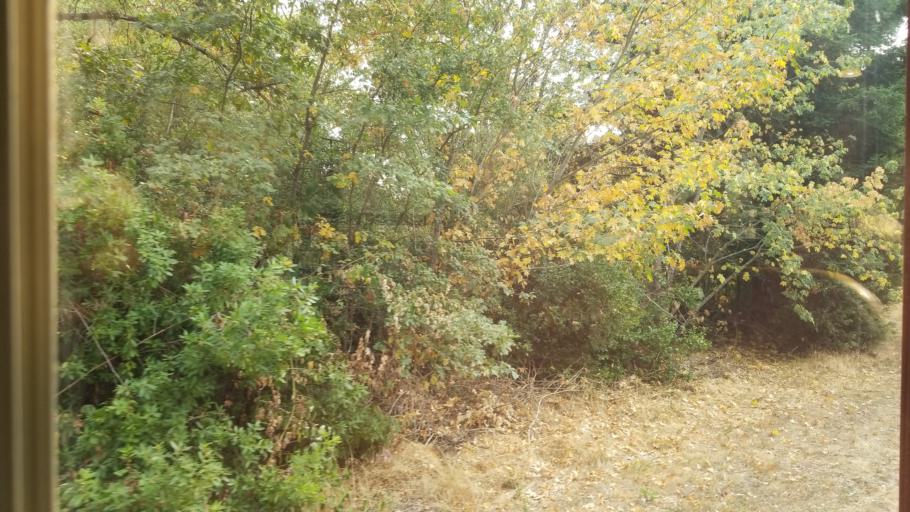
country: US
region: California
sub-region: Mendocino County
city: Willits
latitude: 39.4100
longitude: -123.3505
